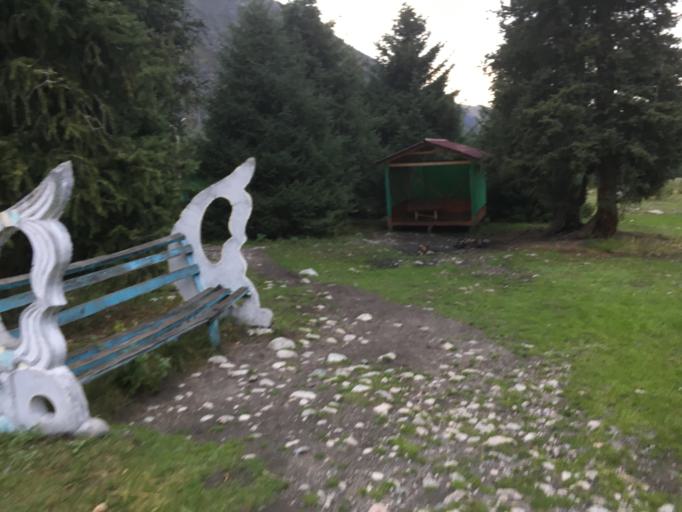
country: KG
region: Chuy
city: Bishkek
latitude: 42.5628
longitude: 74.4826
